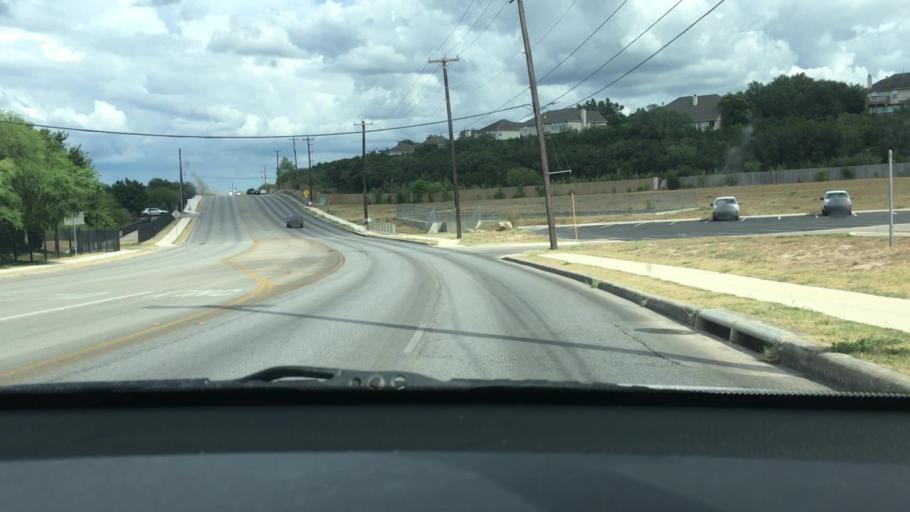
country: US
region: Texas
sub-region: Bexar County
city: Timberwood Park
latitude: 29.6559
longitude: -98.4316
